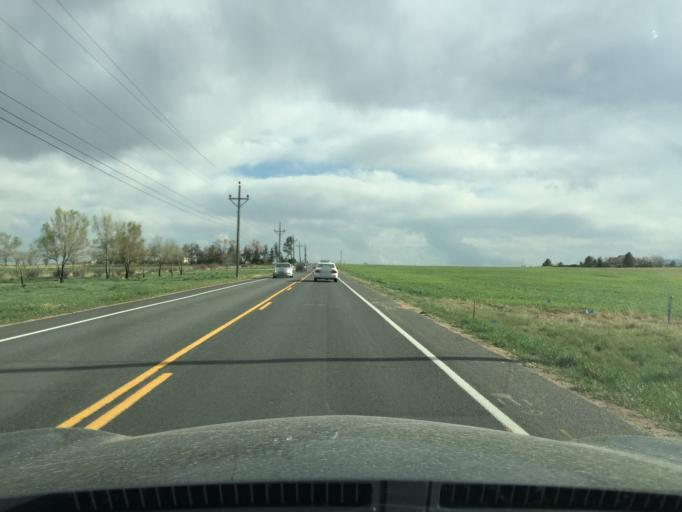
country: US
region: Colorado
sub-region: Boulder County
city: Niwot
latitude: 40.0942
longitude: -105.1316
